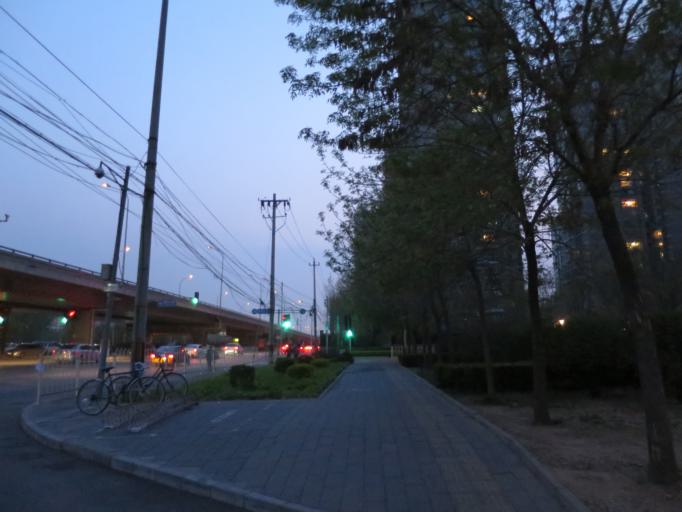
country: CN
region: Beijing
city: Chaowai
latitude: 39.9027
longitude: 116.4455
